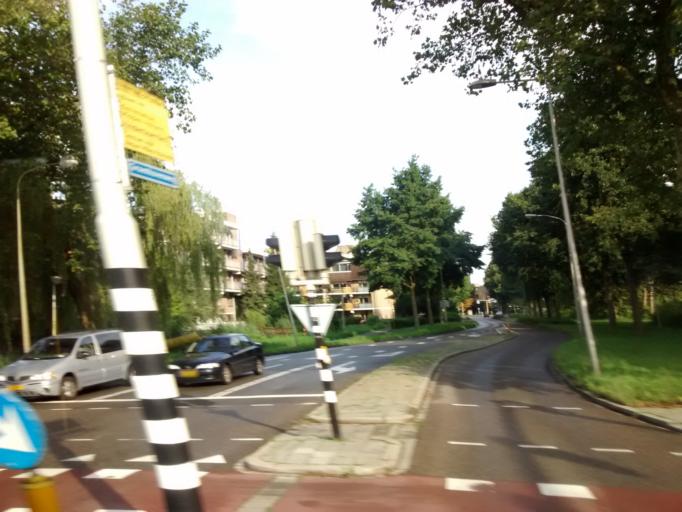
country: NL
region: South Holland
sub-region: Gemeente Gouda
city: Bloemendaal
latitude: 52.0226
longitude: 4.6934
